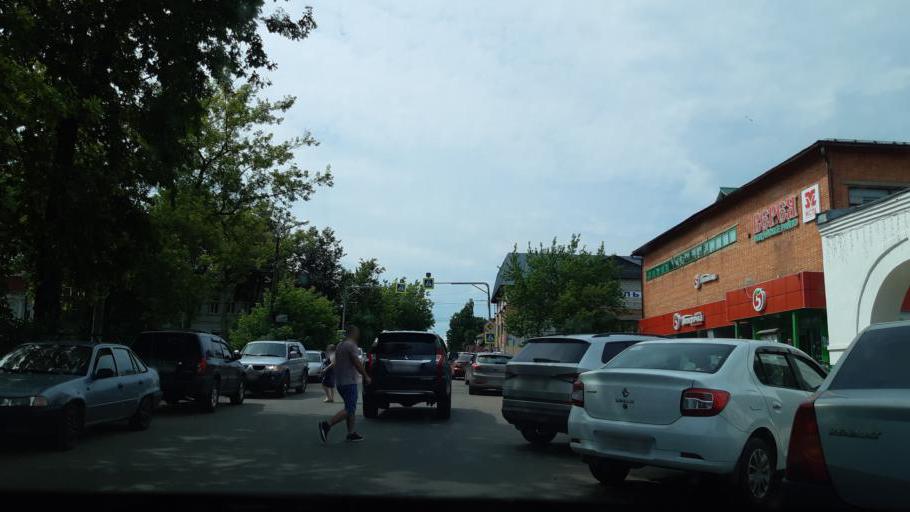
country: RU
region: Moskovskaya
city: Vereya
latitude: 55.3431
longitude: 36.1842
